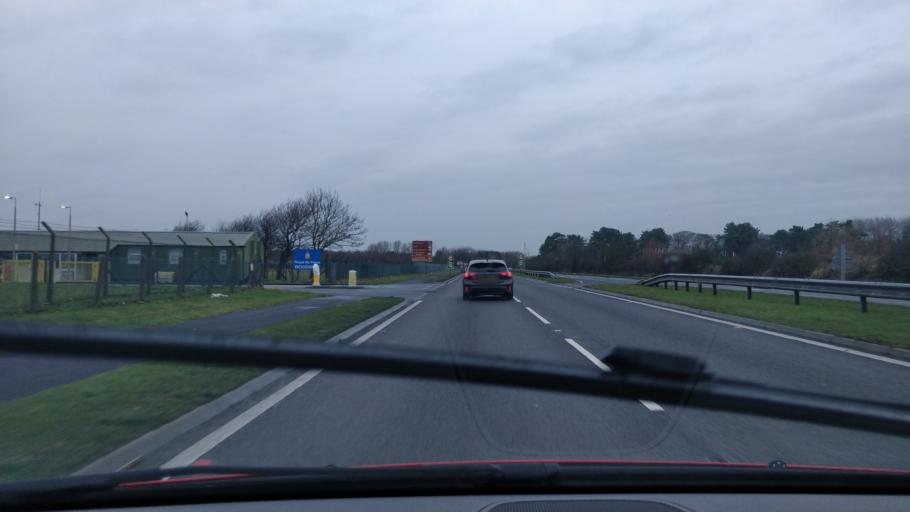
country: GB
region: England
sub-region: Sefton
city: Formby
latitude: 53.5833
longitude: -3.0460
